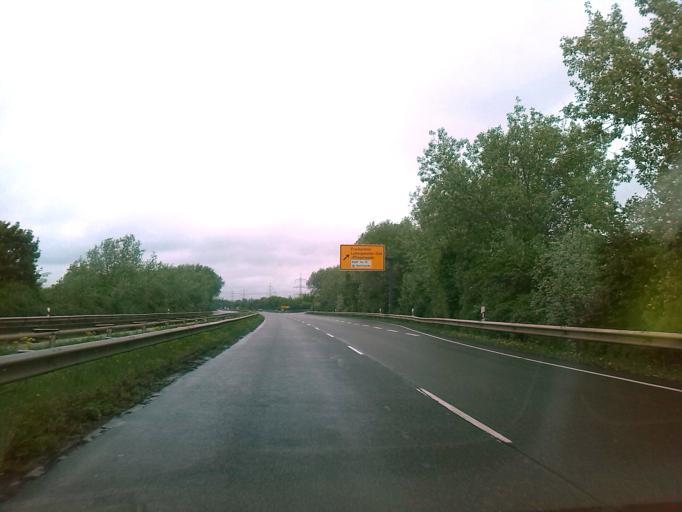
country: DE
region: Rheinland-Pfalz
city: Frankenthal
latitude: 49.5329
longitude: 8.4019
